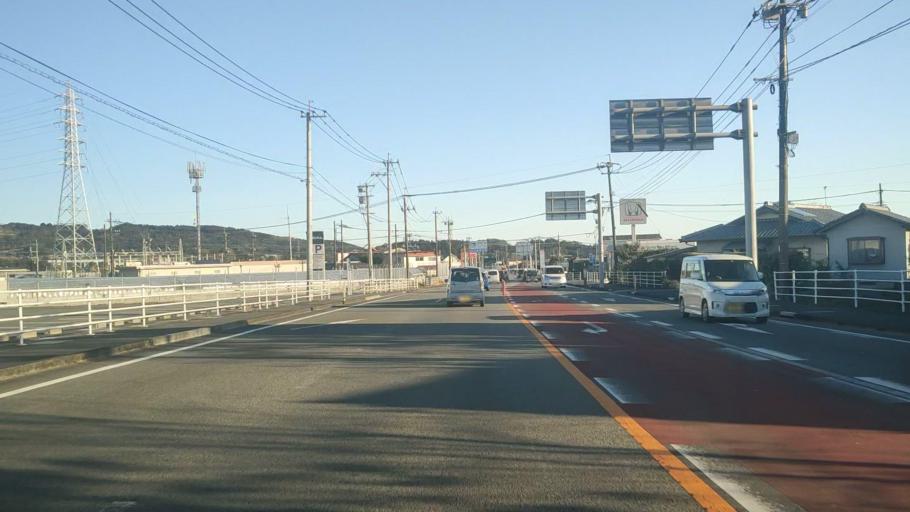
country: JP
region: Miyazaki
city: Takanabe
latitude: 32.2548
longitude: 131.5541
